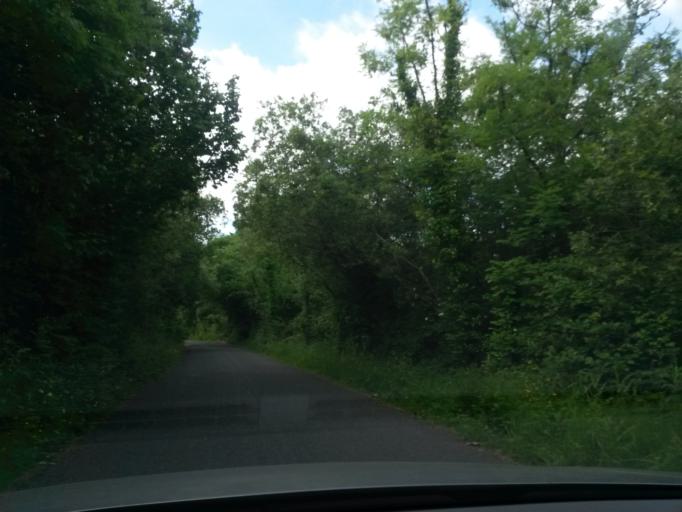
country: IE
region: Connaught
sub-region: Sligo
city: Sligo
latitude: 54.2441
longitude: -8.4439
